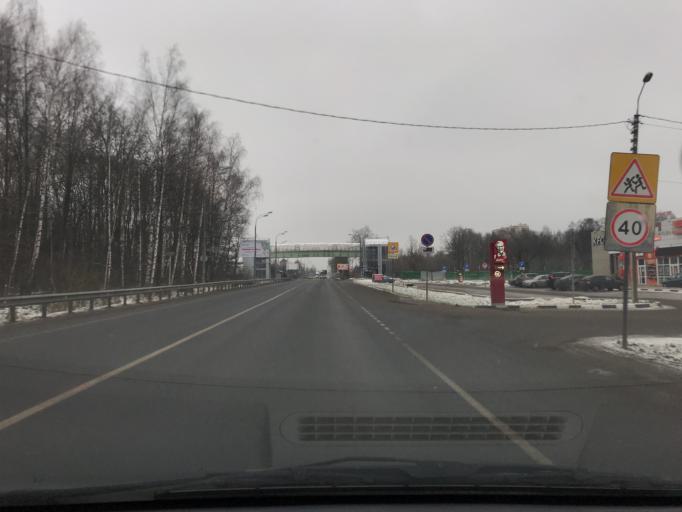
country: RU
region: Moskovskaya
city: Elektrostal'
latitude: 55.8048
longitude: 38.4278
